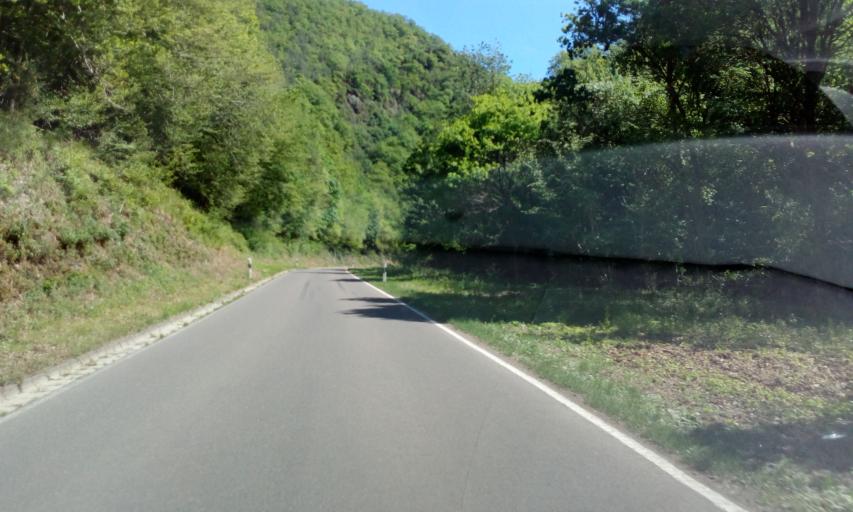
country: DE
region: Rheinland-Pfalz
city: Heidenburg
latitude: 49.8210
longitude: 6.9327
